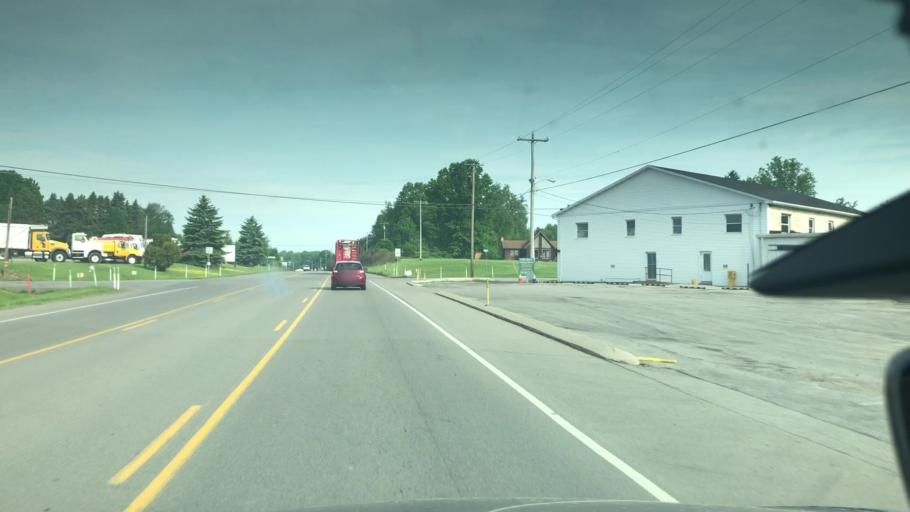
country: US
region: Pennsylvania
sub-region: Butler County
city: Prospect
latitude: 40.9027
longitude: -80.0156
